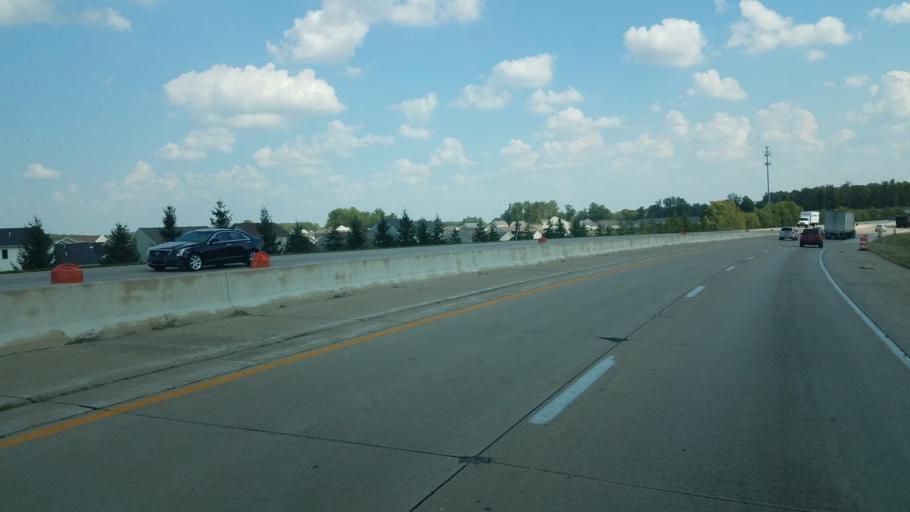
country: US
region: Indiana
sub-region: Allen County
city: Leo-Cedarville
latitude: 41.1540
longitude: -85.0224
